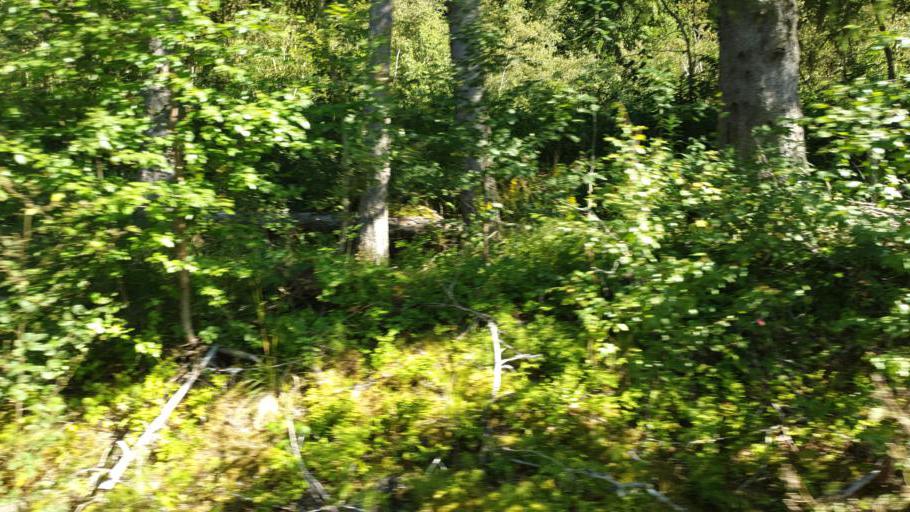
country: NO
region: Sor-Trondelag
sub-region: Meldal
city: Meldal
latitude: 63.1827
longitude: 9.7697
